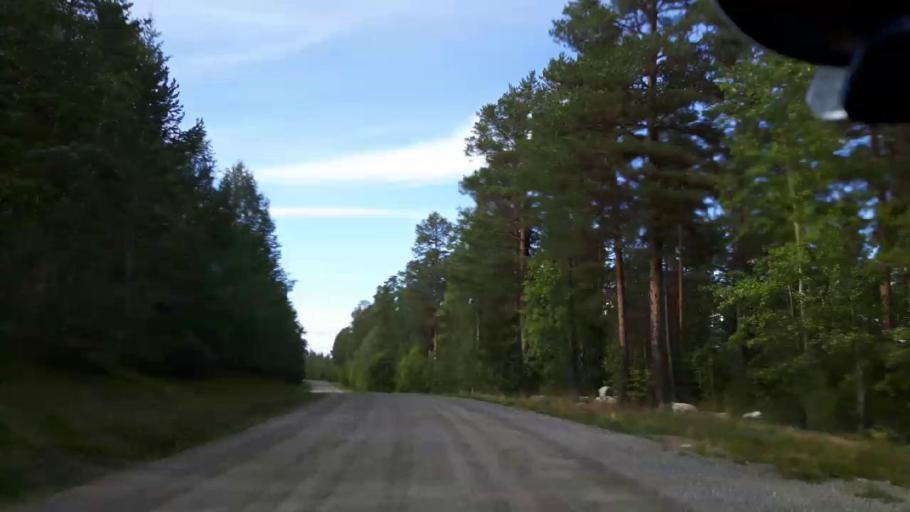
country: SE
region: Jaemtland
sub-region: Ragunda Kommun
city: Hammarstrand
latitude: 63.1485
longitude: 15.8877
